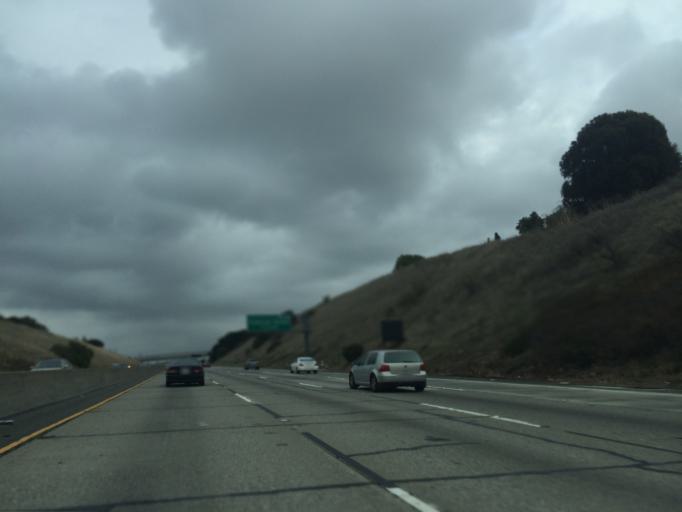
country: US
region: California
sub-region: Contra Costa County
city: Rodeo
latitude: 38.0263
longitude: -122.2589
